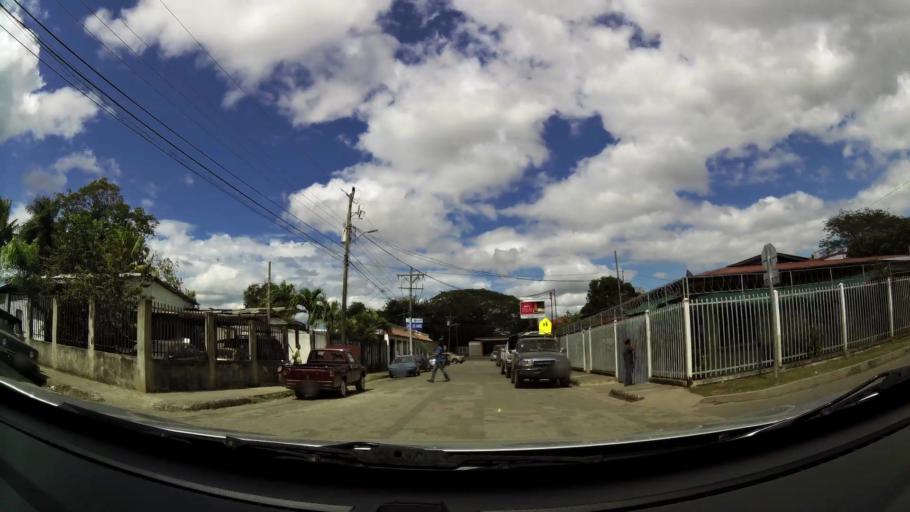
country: CR
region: Guanacaste
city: Santa Cruz
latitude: 10.2628
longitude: -85.5838
